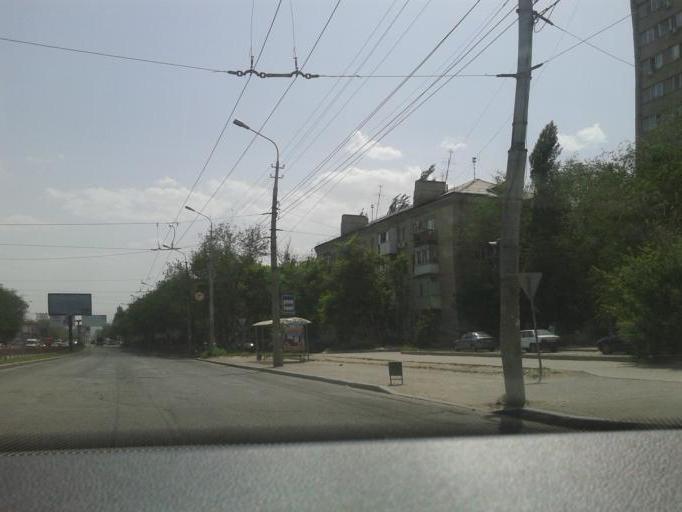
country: RU
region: Volgograd
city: Volgograd
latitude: 48.6153
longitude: 44.4227
